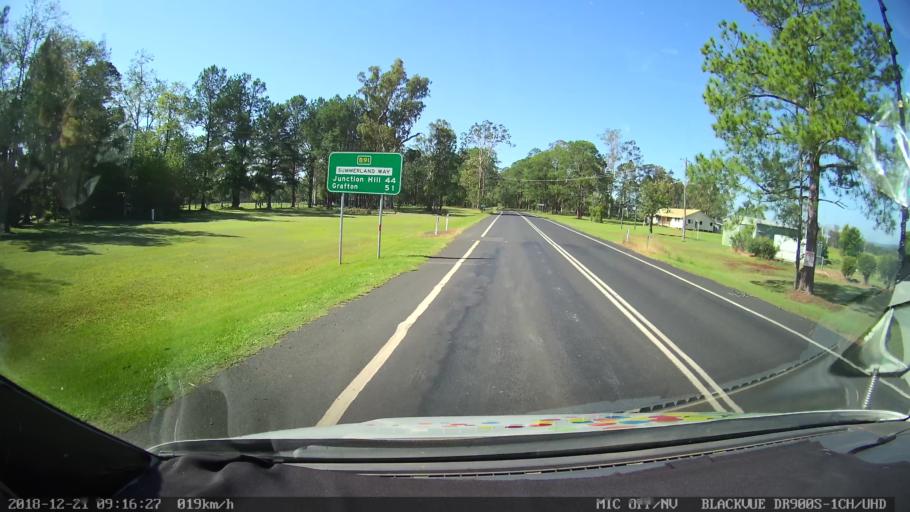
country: AU
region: New South Wales
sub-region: Clarence Valley
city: Maclean
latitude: -29.2830
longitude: 152.9893
